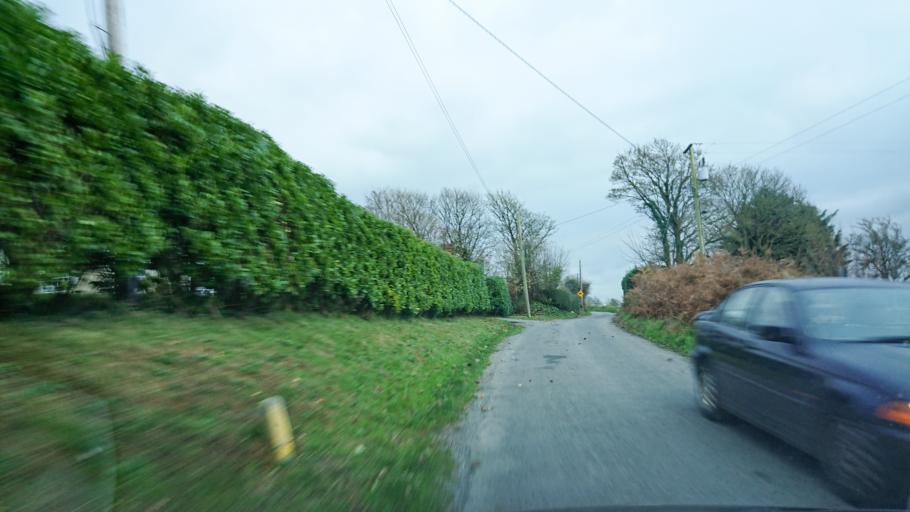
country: IE
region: Munster
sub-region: Waterford
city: Dunmore East
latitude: 52.2511
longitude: -7.0094
